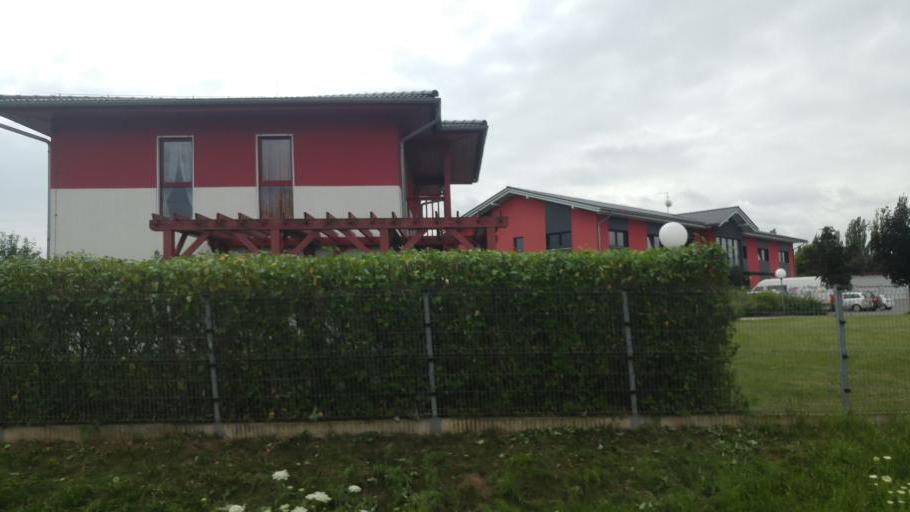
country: CZ
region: Central Bohemia
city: Horomerice
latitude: 50.1413
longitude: 14.3462
